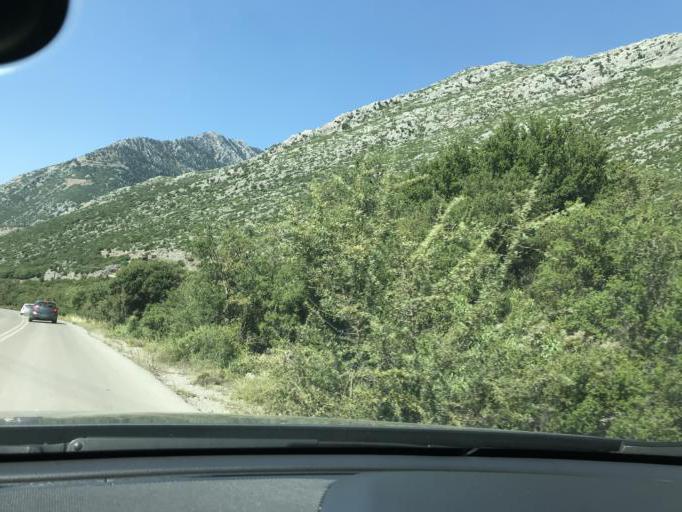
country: GR
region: Central Greece
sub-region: Nomos Voiotias
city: Distomo
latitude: 38.4857
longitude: 22.6892
